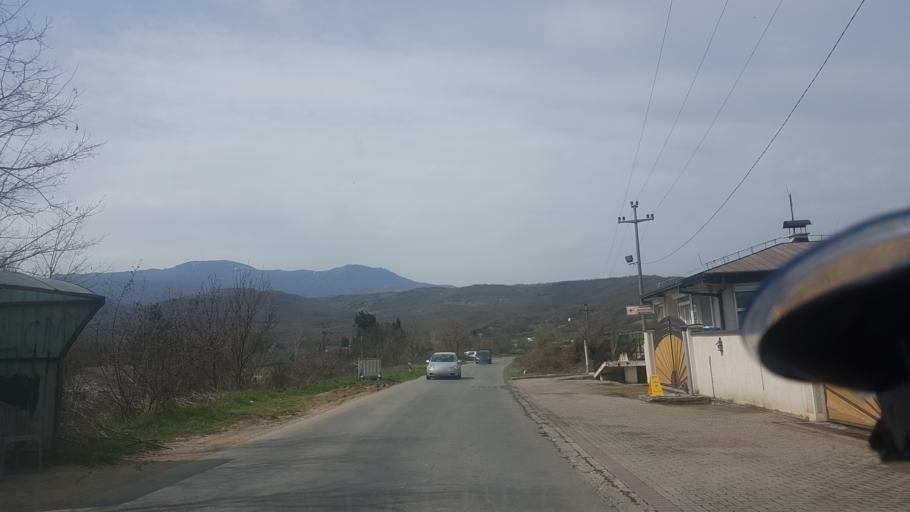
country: MK
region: Zelenikovo
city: Zelenikovo
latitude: 41.8939
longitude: 21.5980
